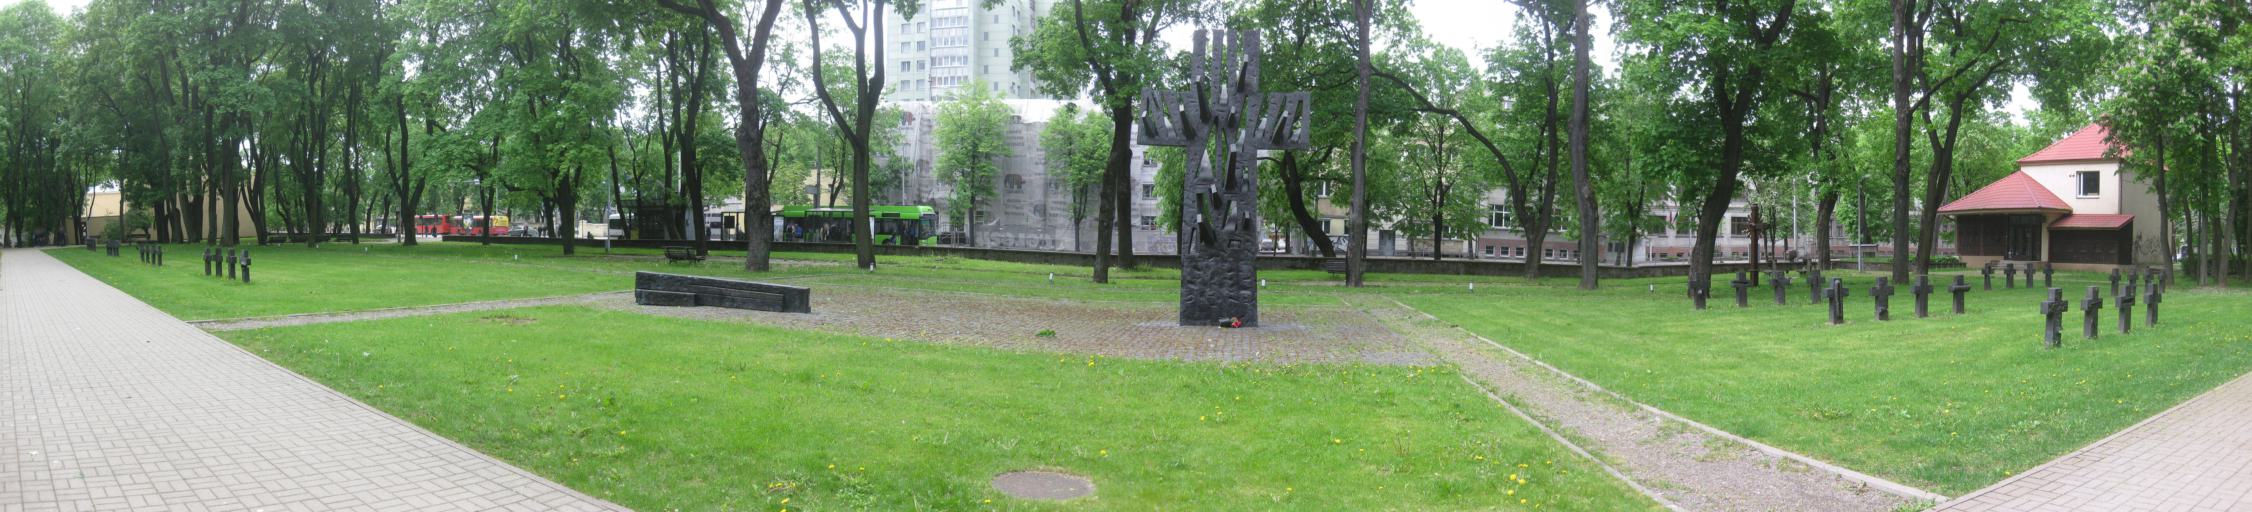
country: LT
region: Kauno apskritis
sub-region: Kaunas
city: Kaunas
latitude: 54.8927
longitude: 23.9259
